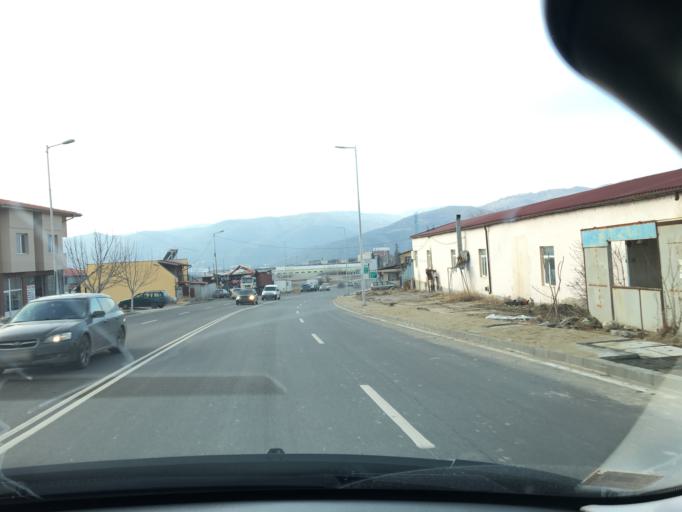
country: BG
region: Blagoevgrad
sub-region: Obshtina Sandanski
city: Sandanski
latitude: 41.5430
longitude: 23.2597
